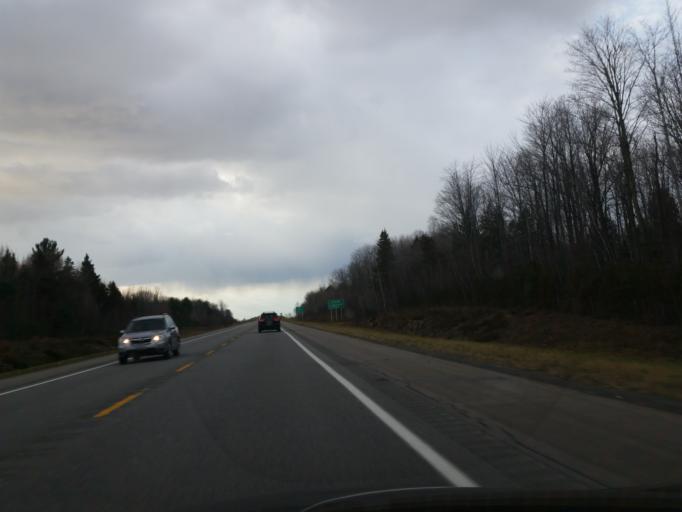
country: CA
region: Quebec
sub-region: Laurentides
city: Lachute
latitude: 45.6411
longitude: -74.2903
